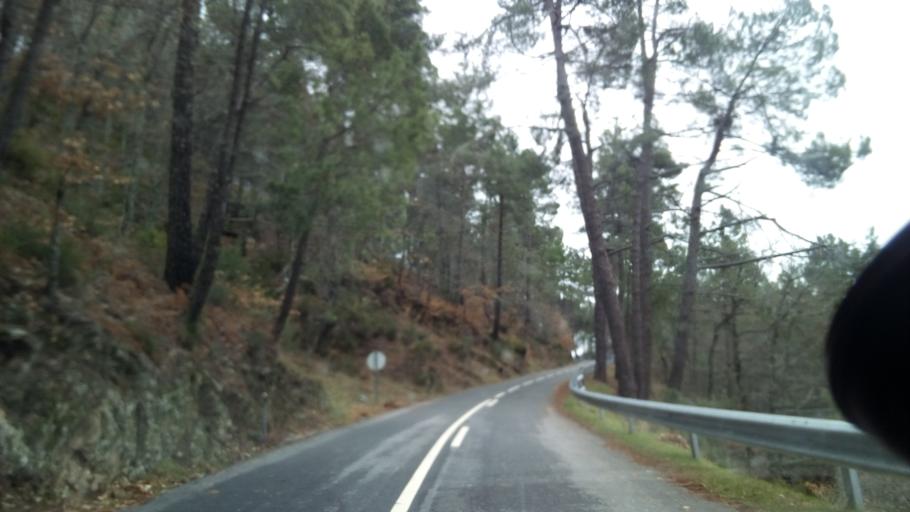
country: PT
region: Guarda
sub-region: Manteigas
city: Manteigas
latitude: 40.4154
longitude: -7.5260
